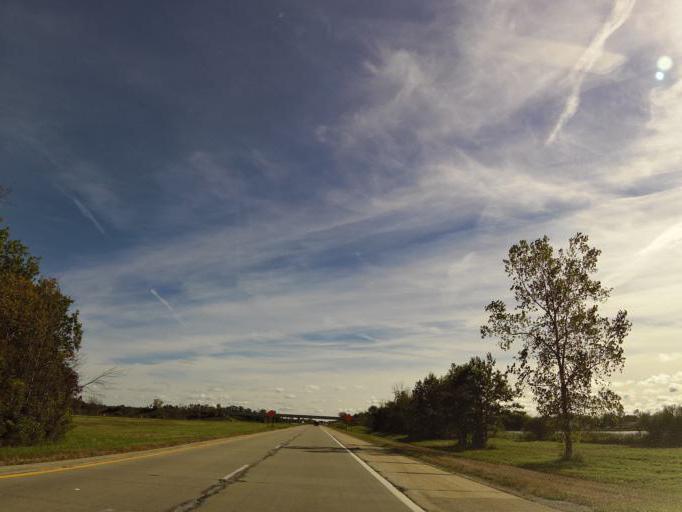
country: US
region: Michigan
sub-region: Macomb County
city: Memphis
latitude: 42.9776
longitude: -82.8088
